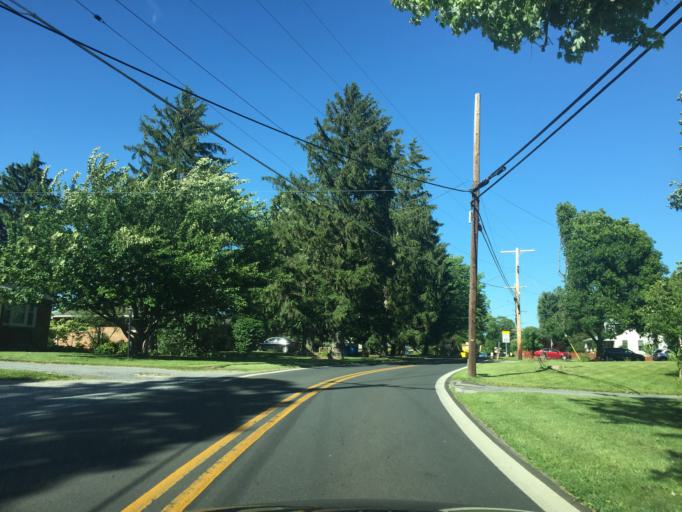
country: US
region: Maryland
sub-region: Carroll County
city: Westminster
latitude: 39.5450
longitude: -76.9227
